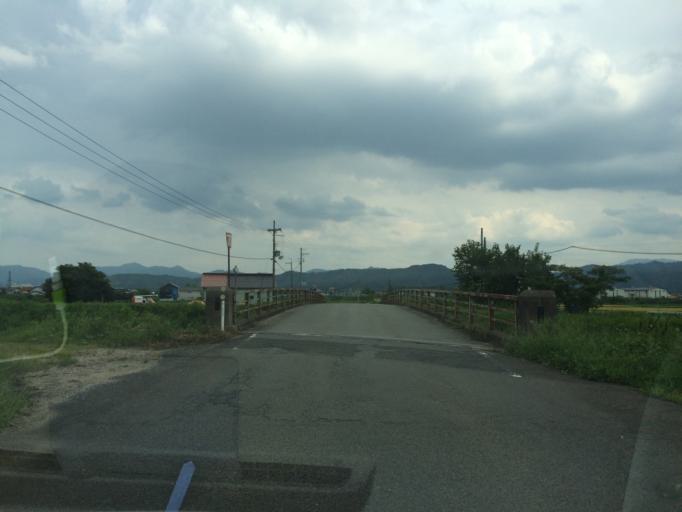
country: JP
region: Hyogo
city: Toyooka
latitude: 35.4970
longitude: 134.7955
